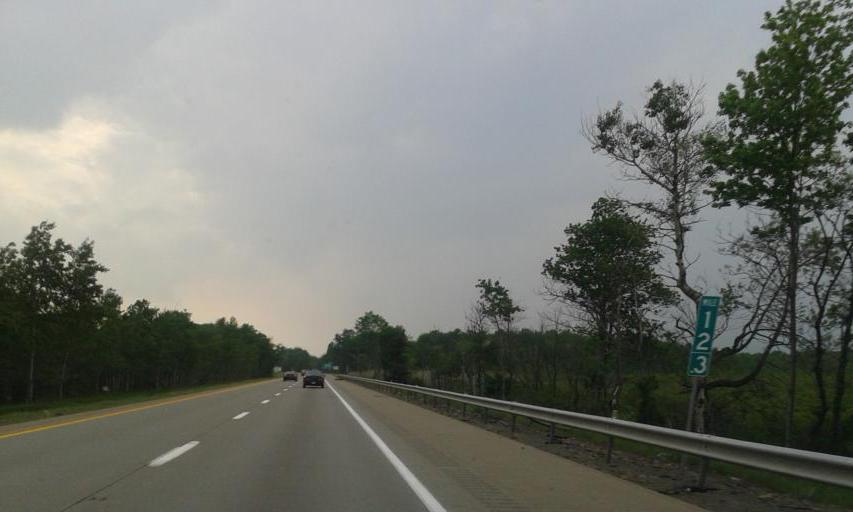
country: US
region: Pennsylvania
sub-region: Lackawanna County
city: Moscow
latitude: 41.2246
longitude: -75.4867
